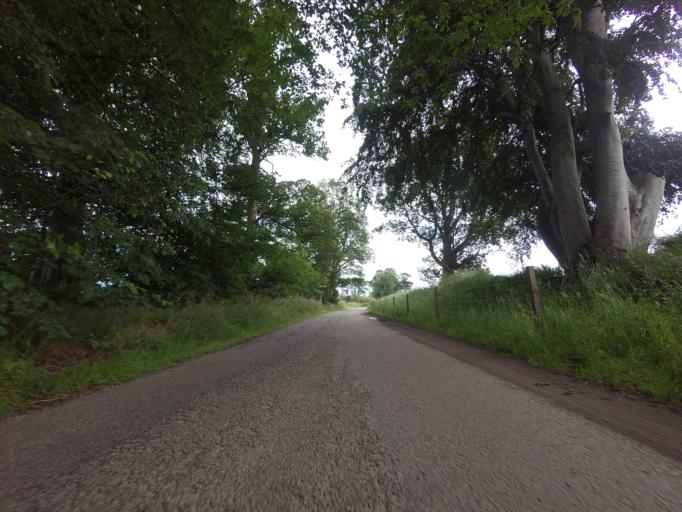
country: GB
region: Scotland
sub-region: Moray
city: Lhanbryd
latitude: 57.6436
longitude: -3.2612
